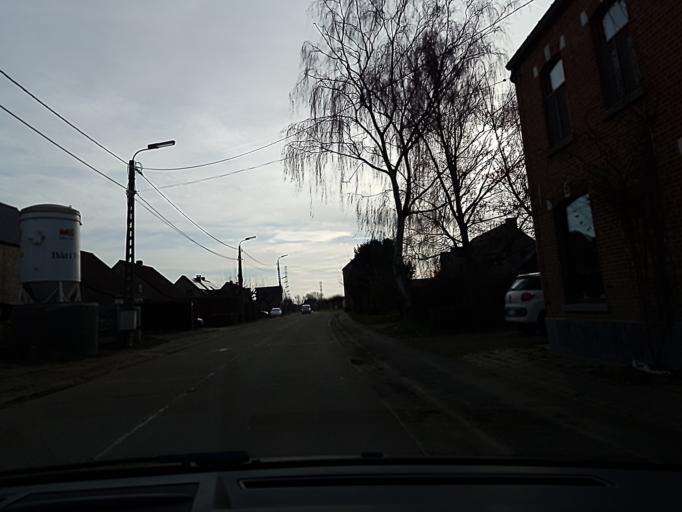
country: BE
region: Flanders
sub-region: Provincie Vlaams-Brabant
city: Rotselaar
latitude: 50.9473
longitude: 4.6800
